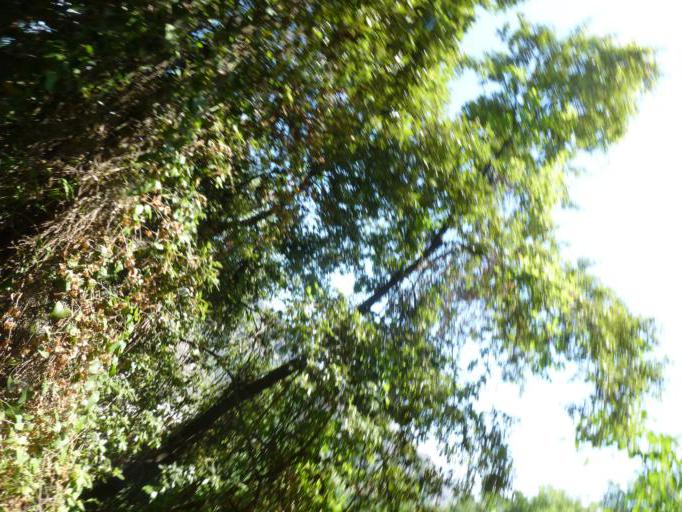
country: IT
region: Calabria
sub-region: Provincia di Reggio Calabria
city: Pazzano
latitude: 38.4803
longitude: 16.4457
